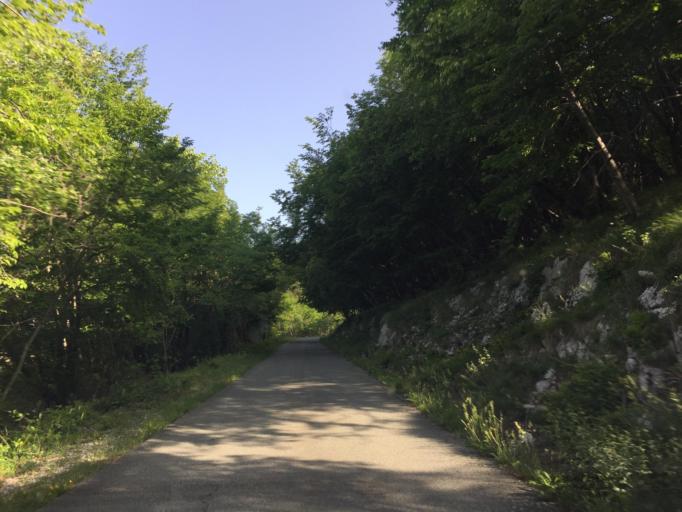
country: HR
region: Primorsko-Goranska
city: Klana
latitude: 45.4930
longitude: 14.4117
